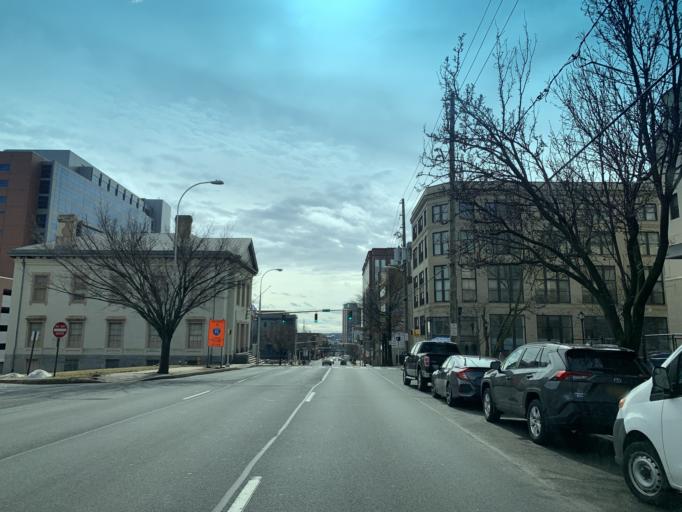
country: US
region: Delaware
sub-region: New Castle County
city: Wilmington
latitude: 39.7420
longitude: -75.5492
